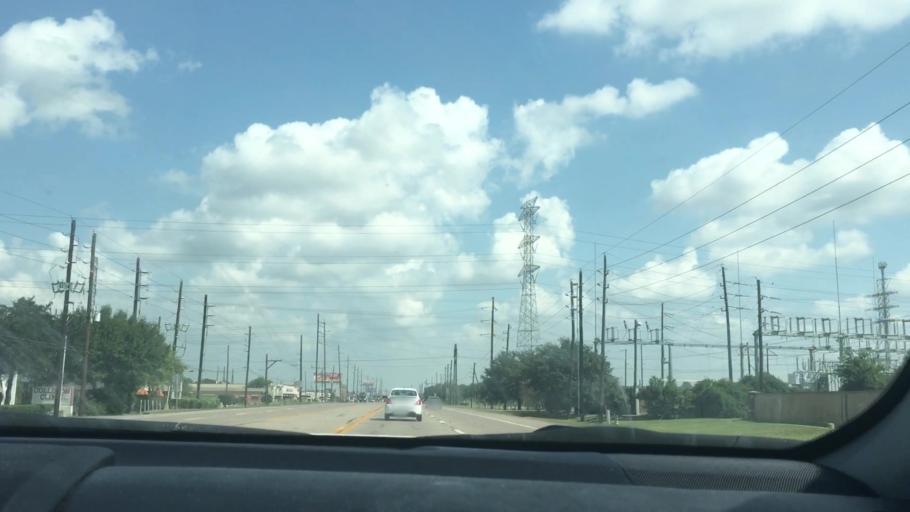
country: US
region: Texas
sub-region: Fort Bend County
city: Fifth Street
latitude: 29.6035
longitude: -95.5643
